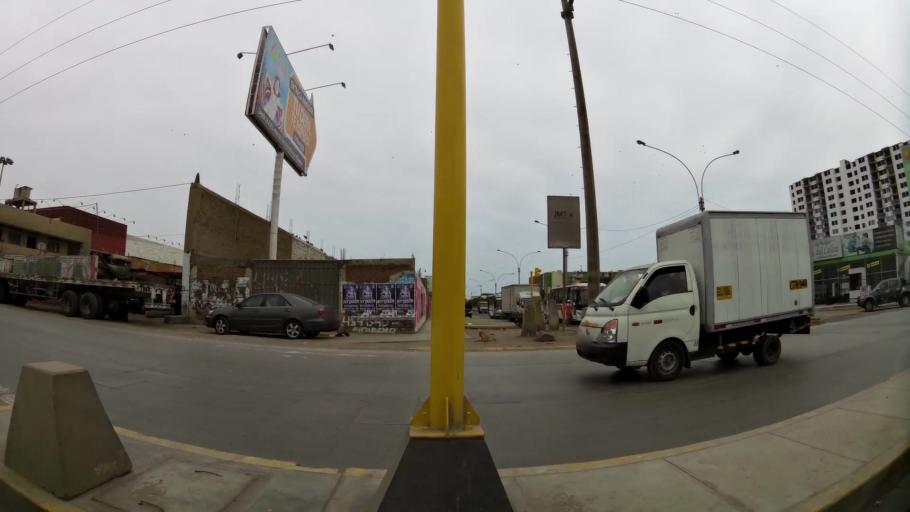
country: PE
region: Callao
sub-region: Callao
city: Callao
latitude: -12.0499
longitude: -77.1151
